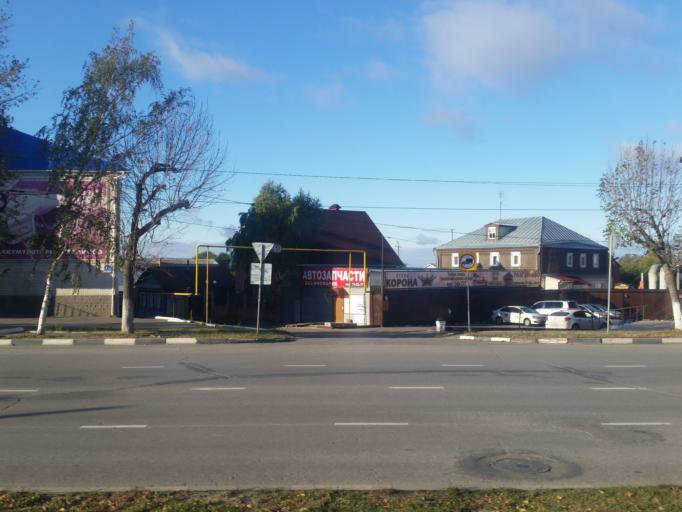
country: RU
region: Ulyanovsk
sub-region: Ulyanovskiy Rayon
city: Ulyanovsk
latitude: 54.3355
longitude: 48.3834
